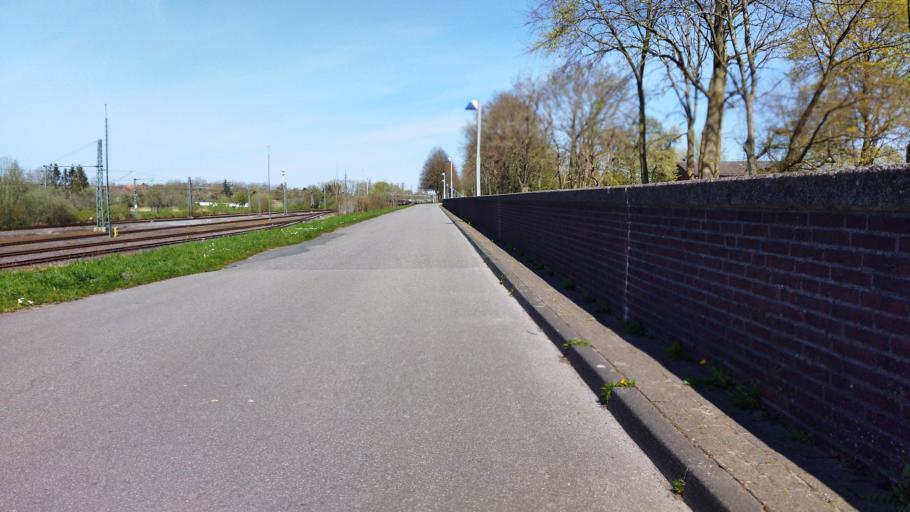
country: DE
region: Lower Saxony
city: Nordenham
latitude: 53.4707
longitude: 8.4791
